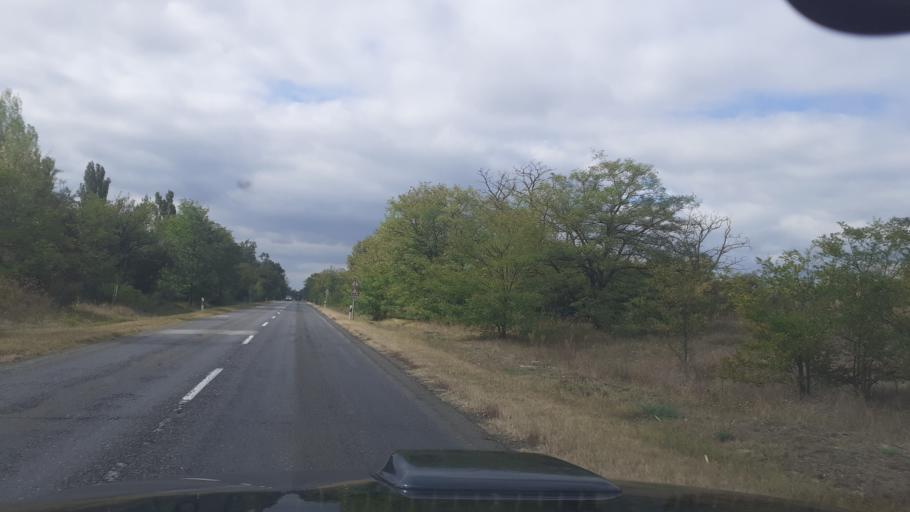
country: HU
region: Bacs-Kiskun
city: Agasegyhaza
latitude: 46.8666
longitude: 19.4061
